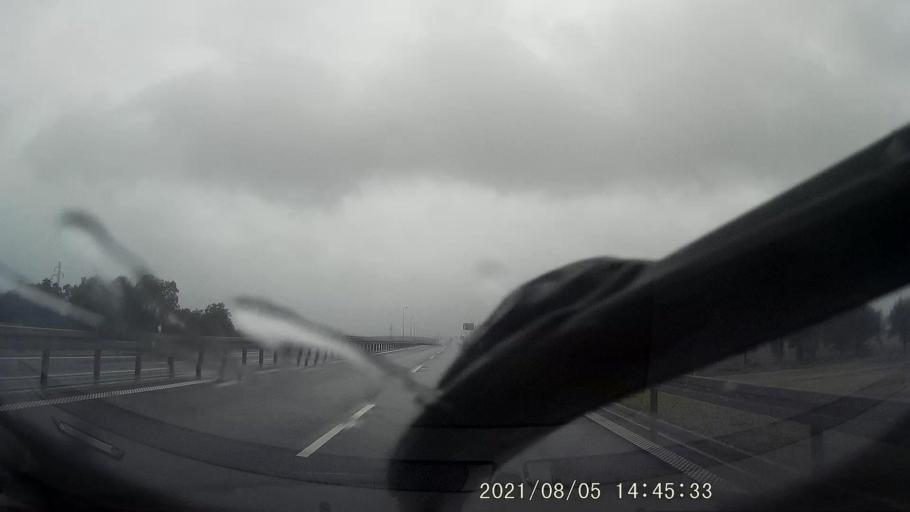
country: PL
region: Opole Voivodeship
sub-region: Powiat nyski
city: Nysa
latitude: 50.4994
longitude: 17.3571
